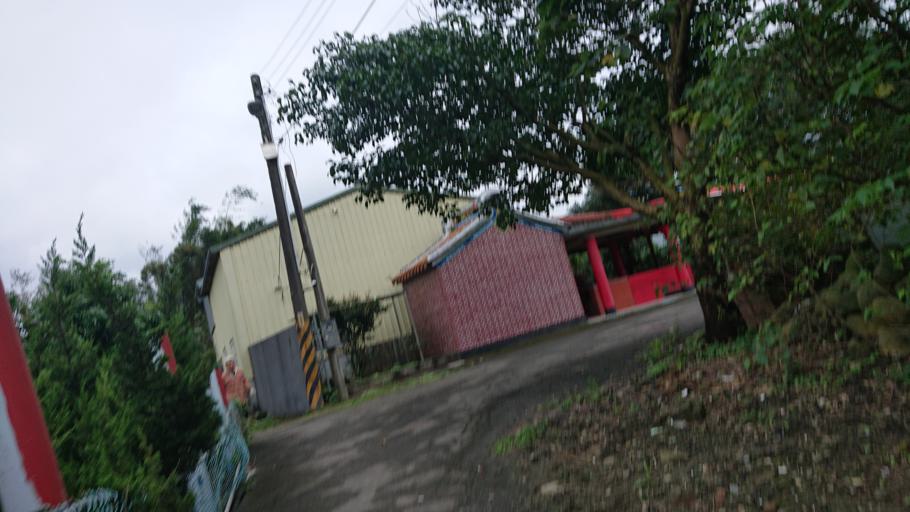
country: TW
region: Taiwan
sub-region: Taoyuan
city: Taoyuan
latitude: 24.9413
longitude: 121.3863
